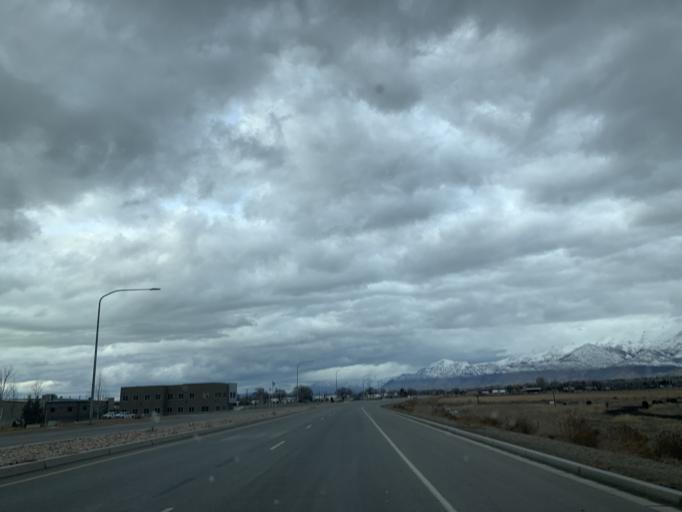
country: US
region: Utah
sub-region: Utah County
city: Provo
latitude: 40.2216
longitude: -111.7126
